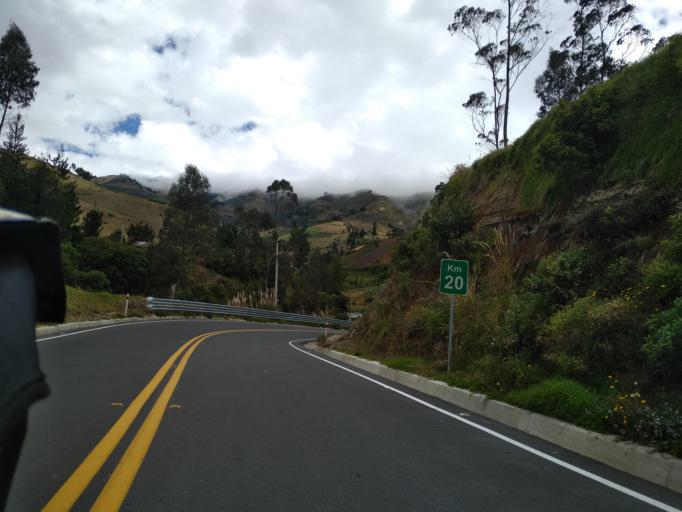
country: EC
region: Cotopaxi
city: Saquisili
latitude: -0.7846
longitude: -78.9113
